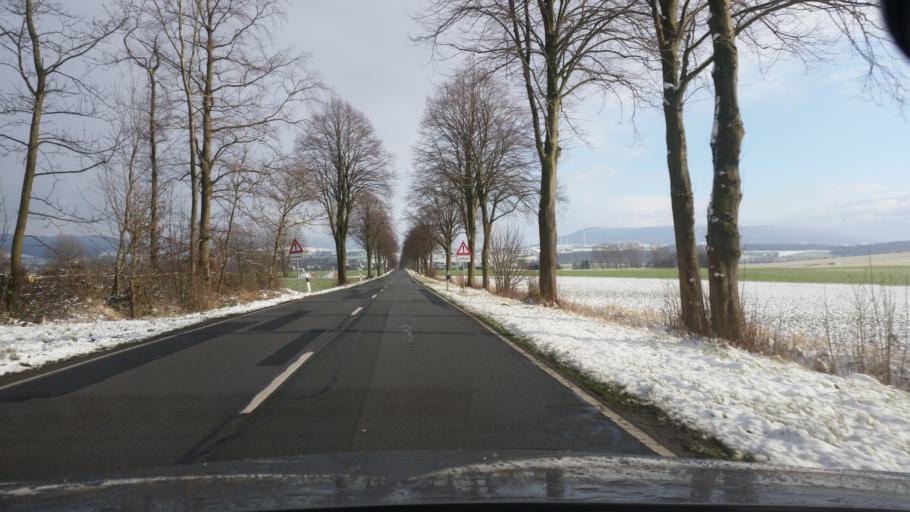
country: DE
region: Lower Saxony
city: Bad Munder am Deister
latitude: 52.1473
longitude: 9.4212
